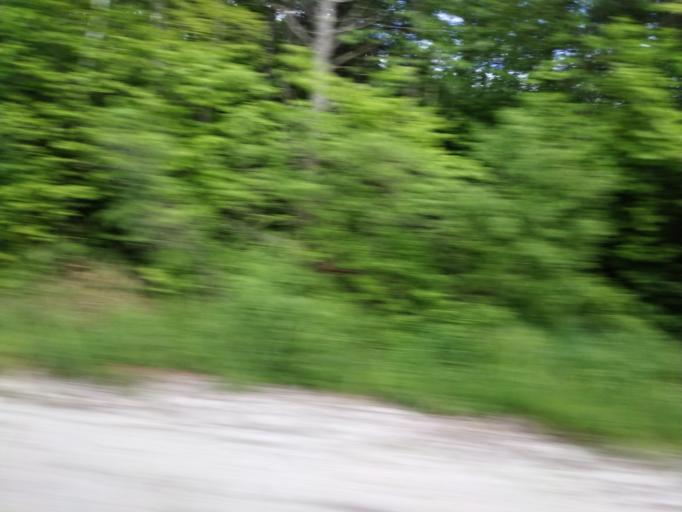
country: US
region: Maine
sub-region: Cumberland County
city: New Gloucester
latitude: 43.8965
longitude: -70.2625
